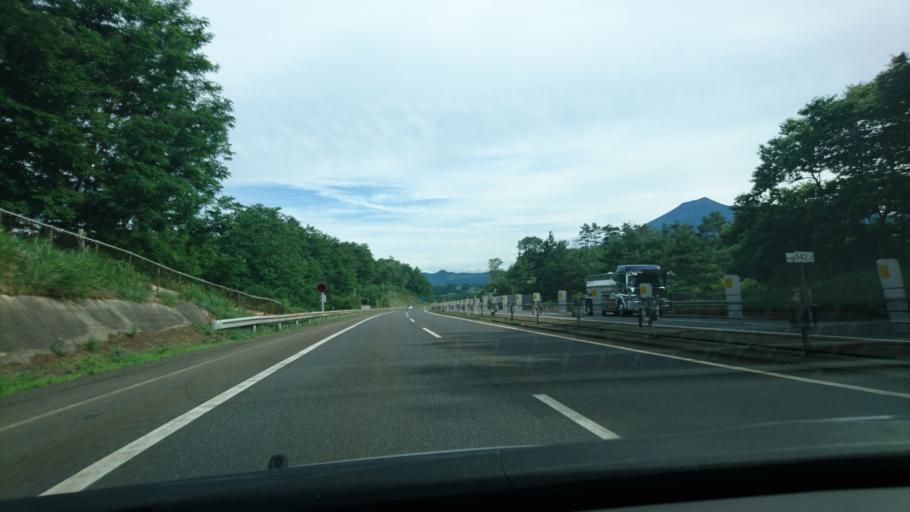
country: JP
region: Iwate
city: Shizukuishi
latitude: 39.9636
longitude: 141.0310
